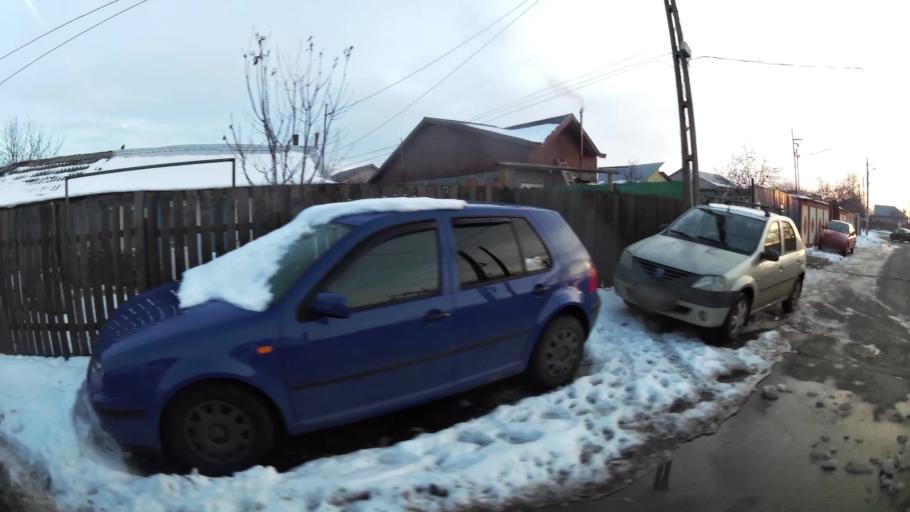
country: RO
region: Ilfov
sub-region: Comuna Magurele
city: Magurele
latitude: 44.3897
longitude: 26.0329
